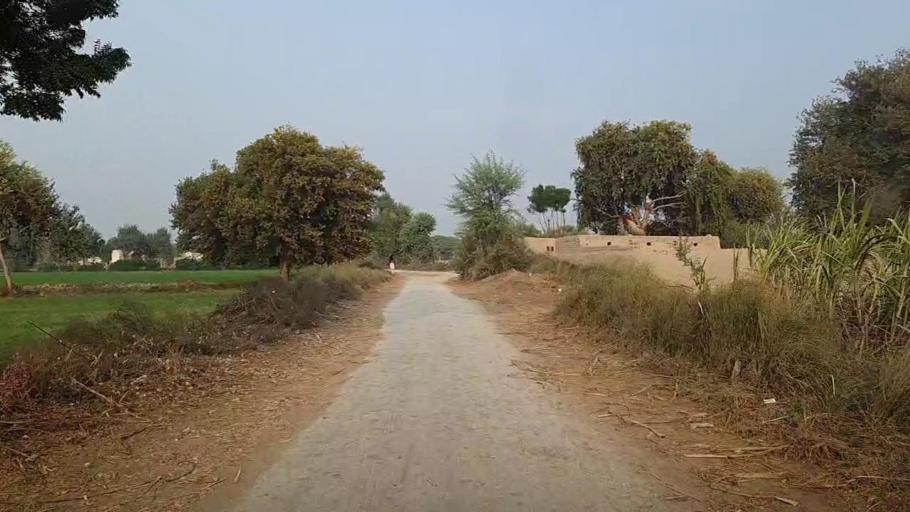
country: PK
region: Sindh
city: Setharja Old
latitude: 27.0958
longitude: 68.5013
